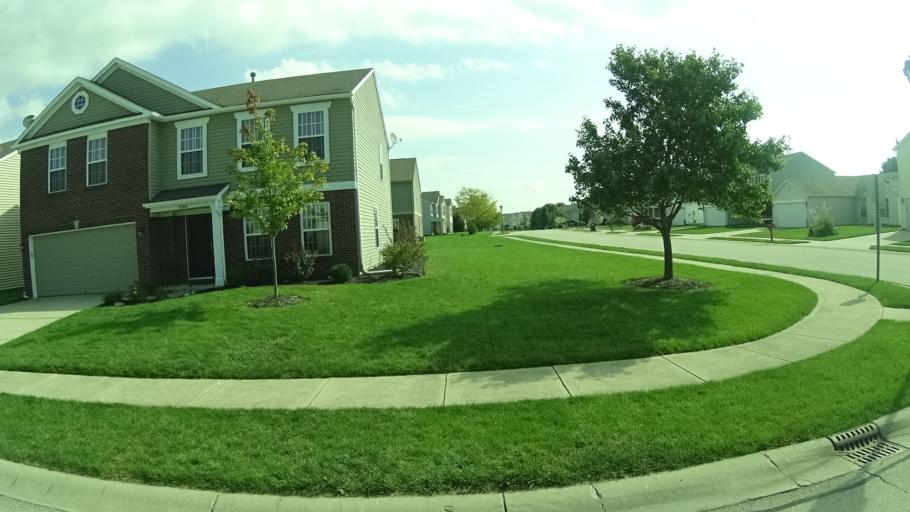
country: US
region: Indiana
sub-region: Hancock County
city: Fortville
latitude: 39.9825
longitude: -85.8540
